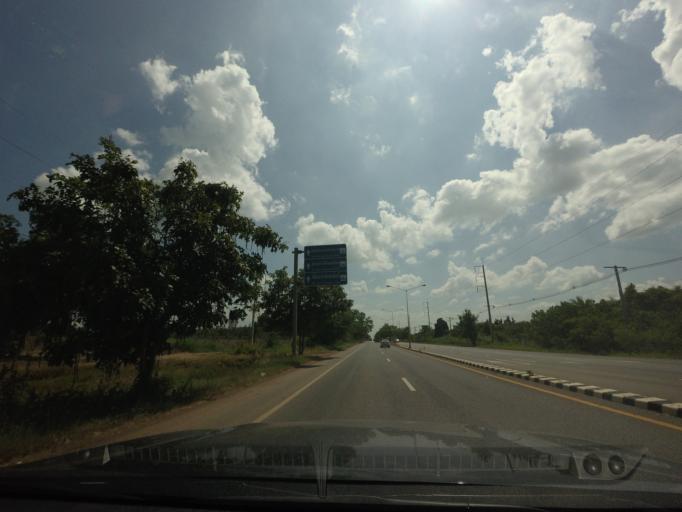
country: TH
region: Phetchabun
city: Nong Phai
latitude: 16.0207
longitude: 101.0734
